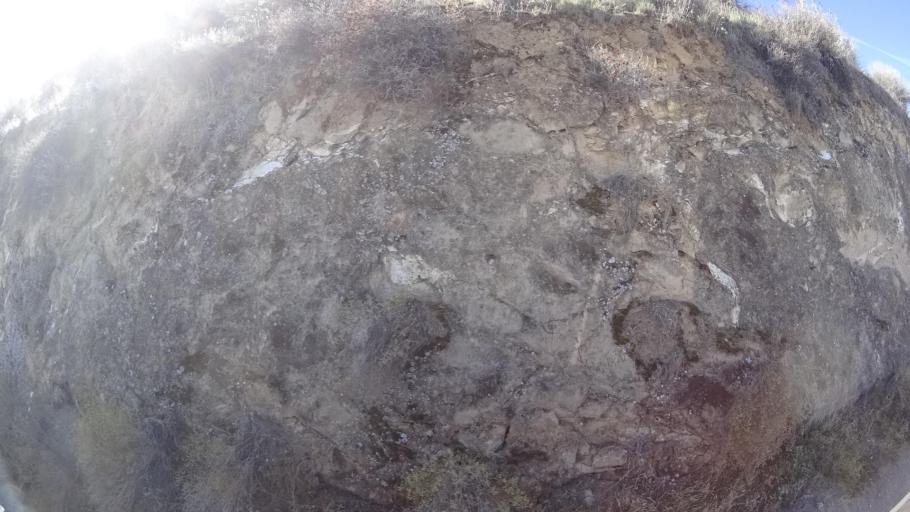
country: US
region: California
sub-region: Kern County
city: Maricopa
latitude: 35.0138
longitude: -119.4685
